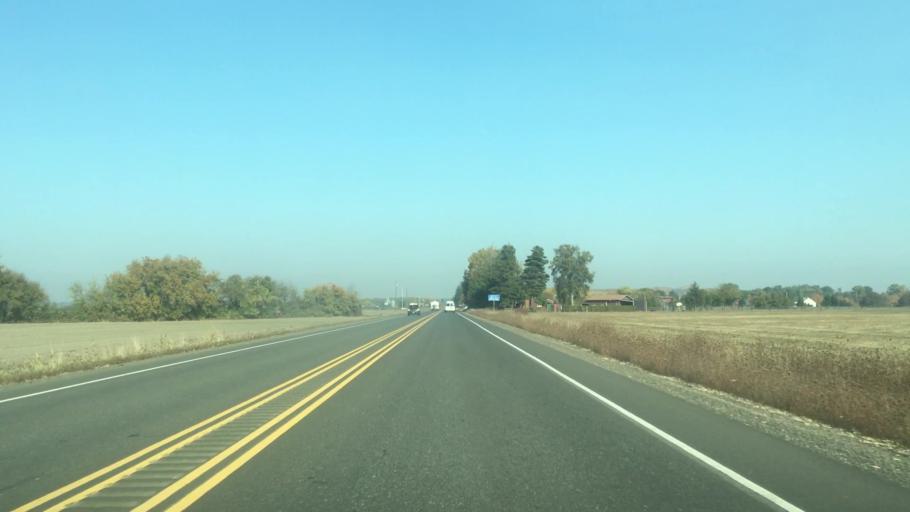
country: US
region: Oregon
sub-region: Yamhill County
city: Amity
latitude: 45.1497
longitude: -123.2736
